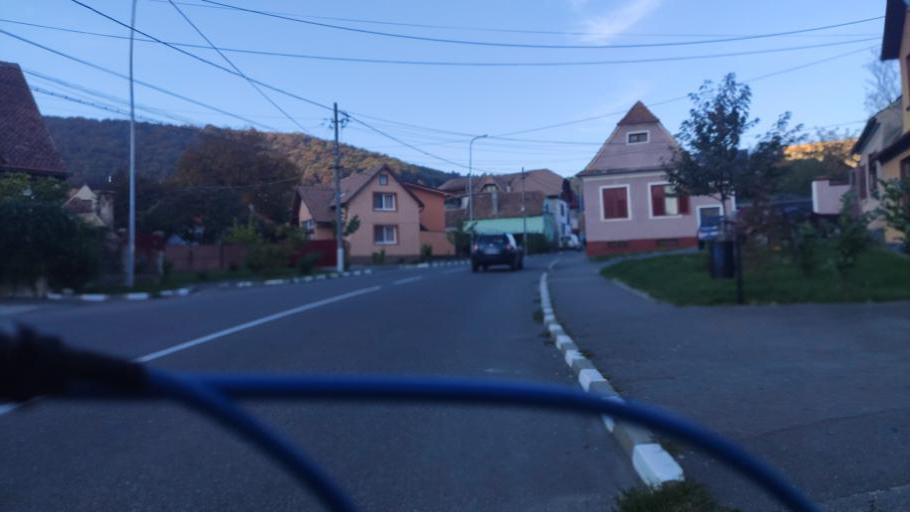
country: RO
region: Brasov
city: Codlea
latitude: 45.7028
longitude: 25.4410
